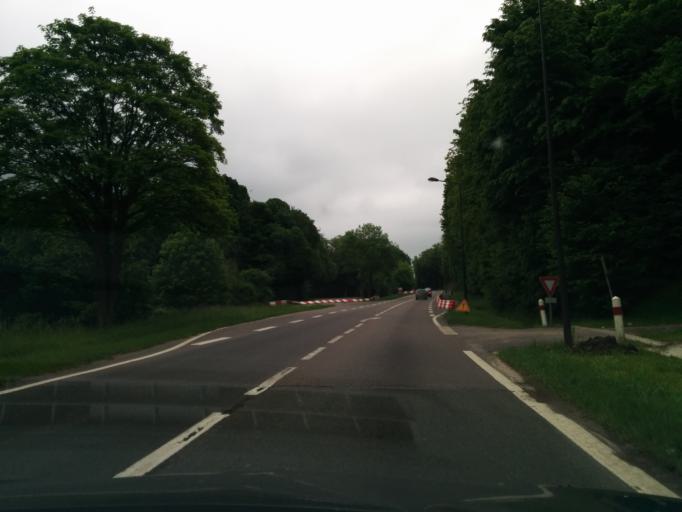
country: FR
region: Ile-de-France
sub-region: Departement des Yvelines
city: Rosny-sur-Seine
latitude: 49.0072
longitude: 1.6167
